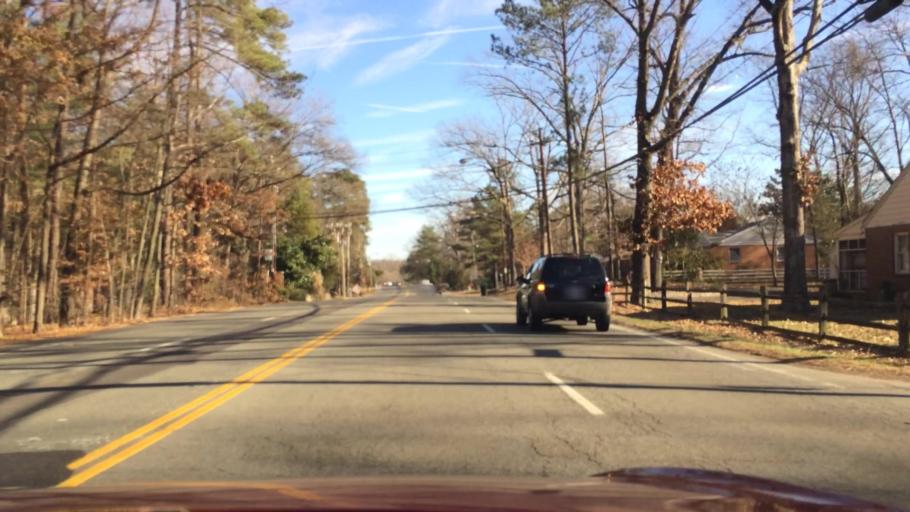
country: US
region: Virginia
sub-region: Chesterfield County
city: Bon Air
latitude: 37.5367
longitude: -77.5151
